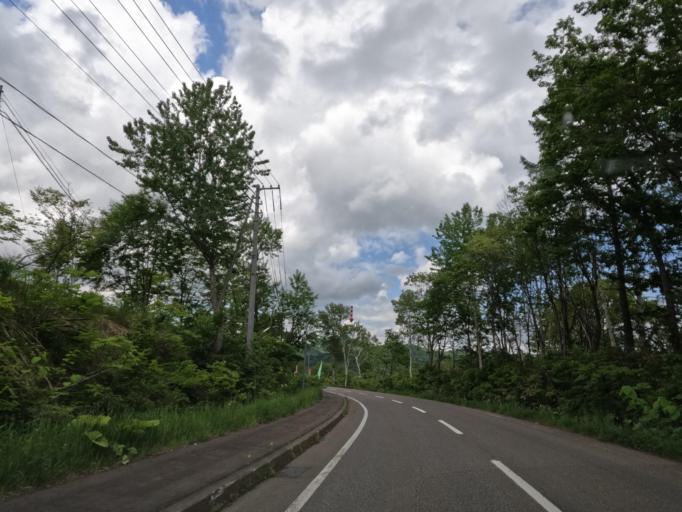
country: JP
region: Hokkaido
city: Takikawa
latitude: 43.5845
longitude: 141.7310
